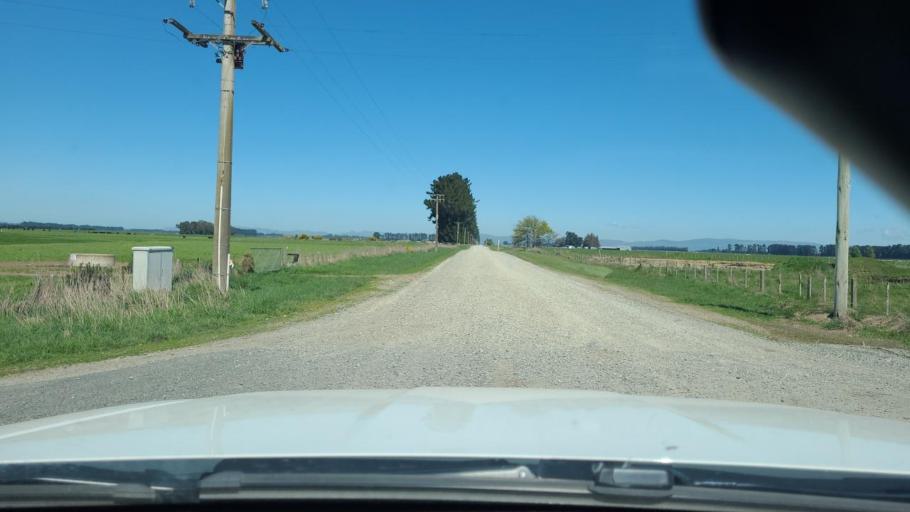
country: NZ
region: Southland
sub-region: Gore District
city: Gore
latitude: -45.7595
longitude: 168.7104
